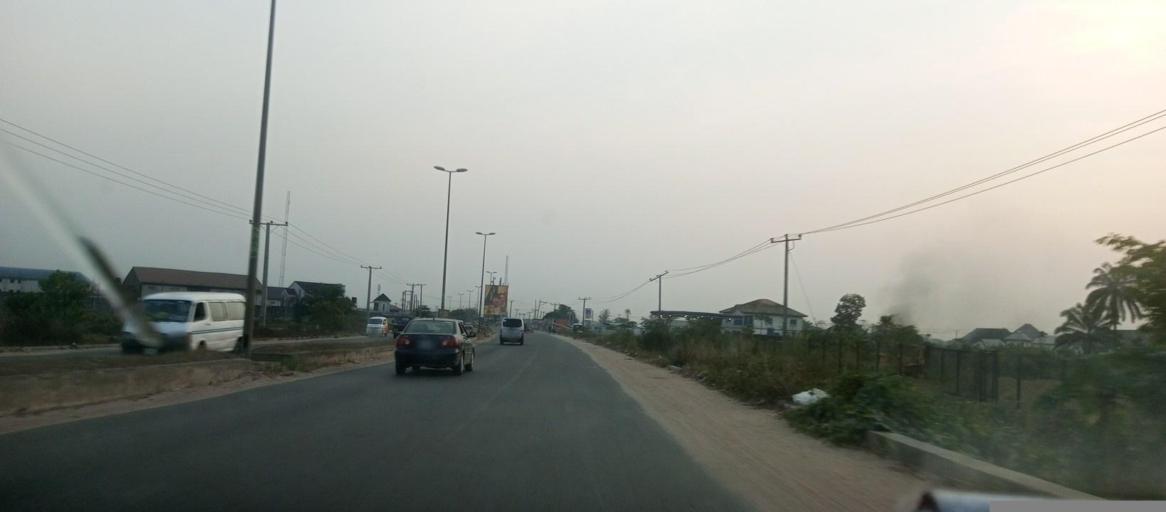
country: NG
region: Rivers
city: Emuoha
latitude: 4.9234
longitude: 6.9975
